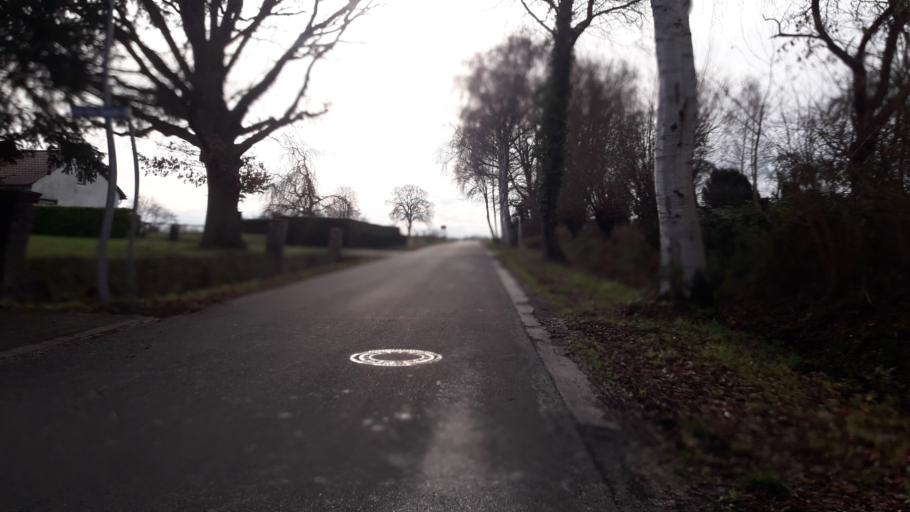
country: DE
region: North Rhine-Westphalia
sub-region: Regierungsbezirk Arnsberg
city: Soest
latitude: 51.5822
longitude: 8.0582
